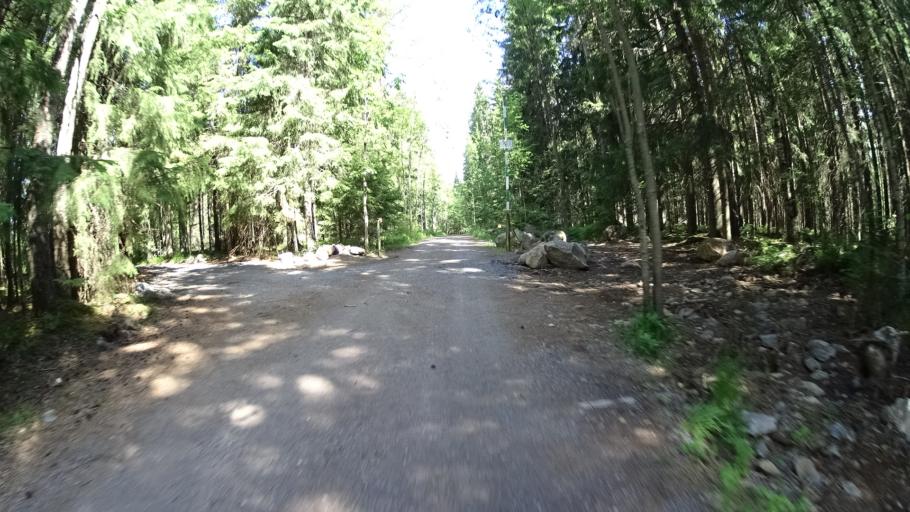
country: FI
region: Uusimaa
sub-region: Helsinki
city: Vihti
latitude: 60.3194
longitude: 24.4479
